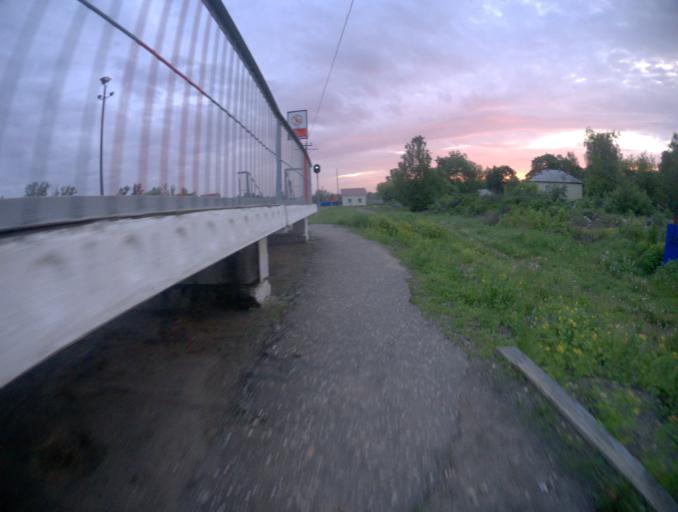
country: RU
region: Vladimir
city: Gus'-Khrustal'nyy
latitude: 55.6195
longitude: 40.6503
